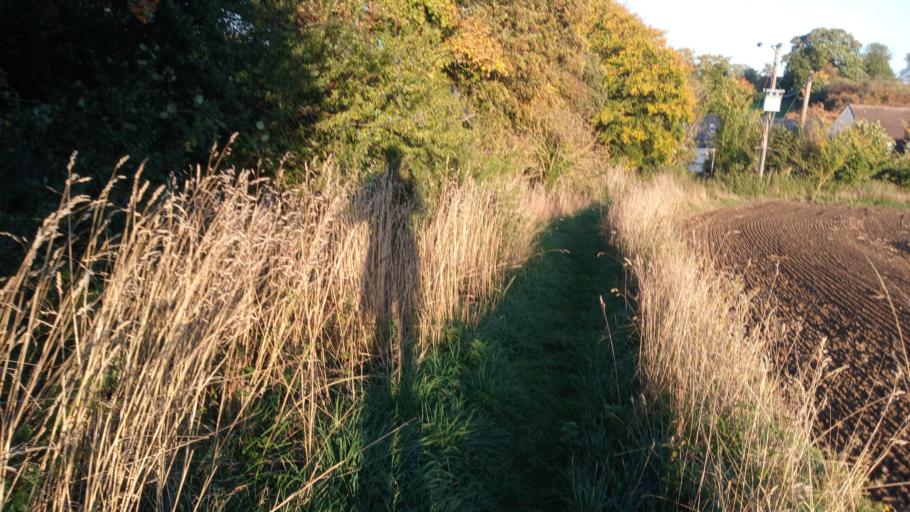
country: GB
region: England
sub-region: Cambridgeshire
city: Linton
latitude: 52.0527
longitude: 0.3098
